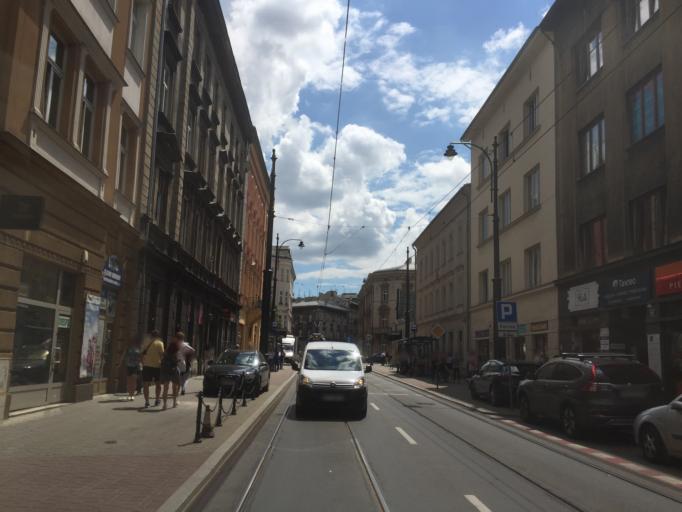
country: PL
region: Lesser Poland Voivodeship
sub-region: Krakow
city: Krakow
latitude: 50.0699
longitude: 19.9373
